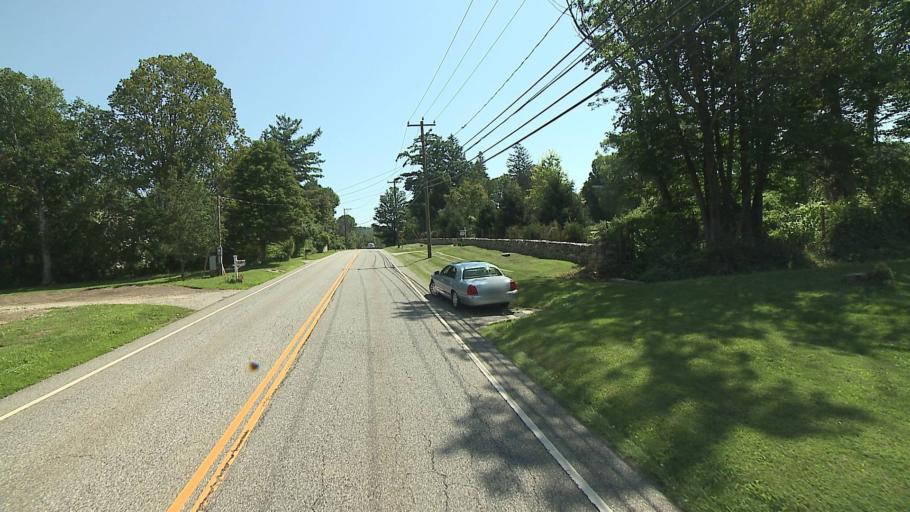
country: US
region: Connecticut
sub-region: Litchfield County
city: Kent
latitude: 41.8760
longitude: -73.4718
